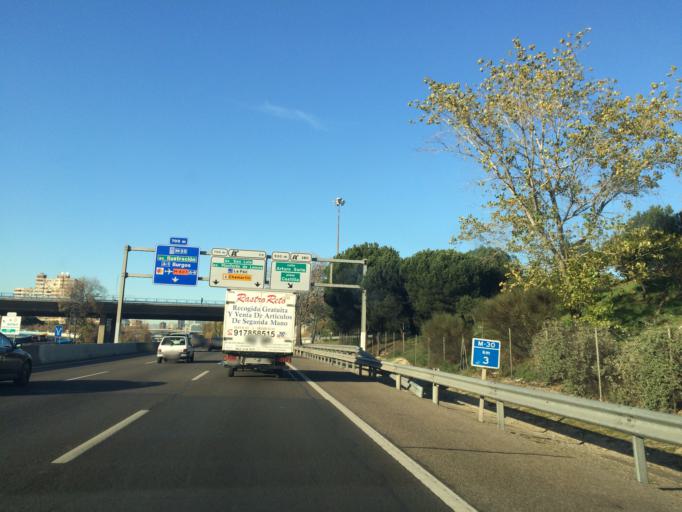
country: ES
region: Madrid
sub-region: Provincia de Madrid
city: Chamartin
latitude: 40.4589
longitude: -3.6639
